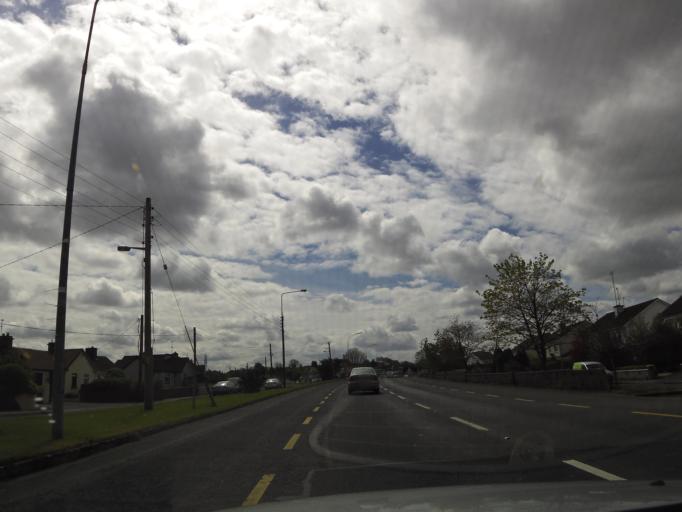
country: IE
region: Connaught
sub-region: County Galway
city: Tuam
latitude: 53.5251
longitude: -8.8513
